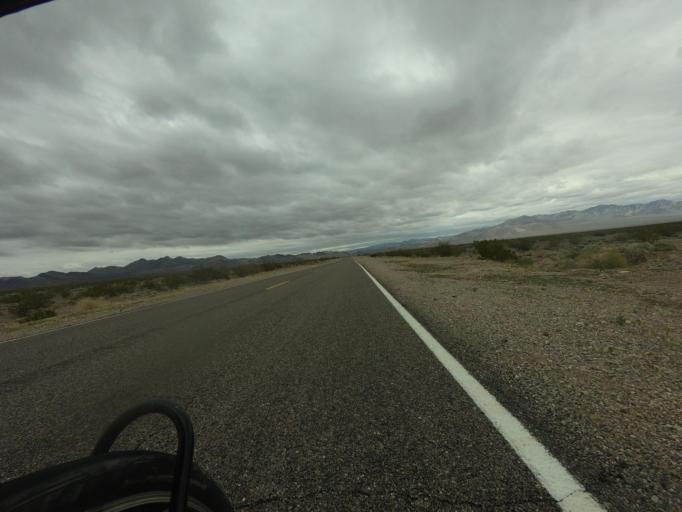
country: US
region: Nevada
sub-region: Nye County
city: Beatty
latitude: 36.8347
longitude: -116.8771
